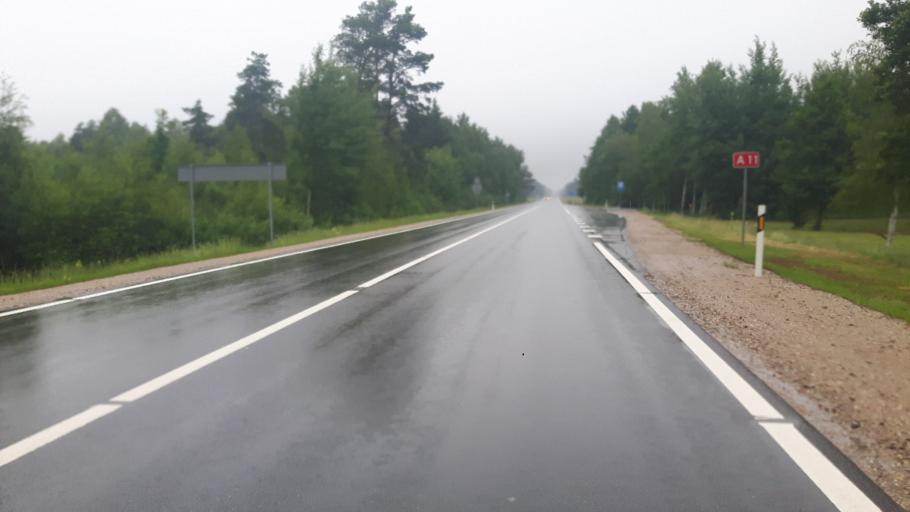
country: LV
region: Rucavas
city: Rucava
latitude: 56.1582
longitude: 21.1473
